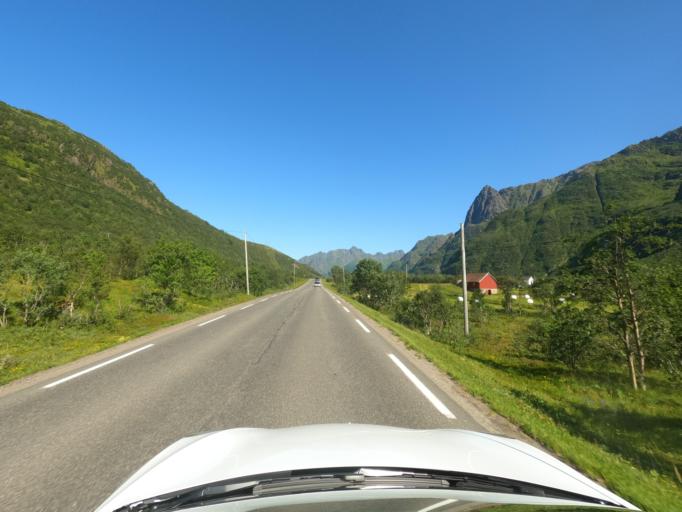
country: NO
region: Nordland
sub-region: Hadsel
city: Melbu
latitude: 68.3695
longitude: 14.7714
